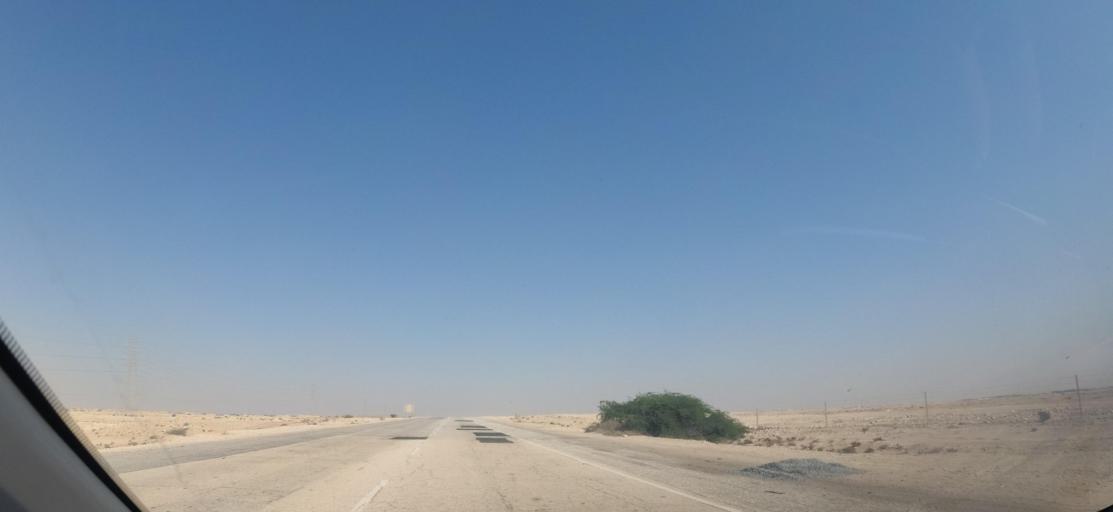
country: QA
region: Baladiyat ar Rayyan
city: Dukhan
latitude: 25.4754
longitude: 50.9439
